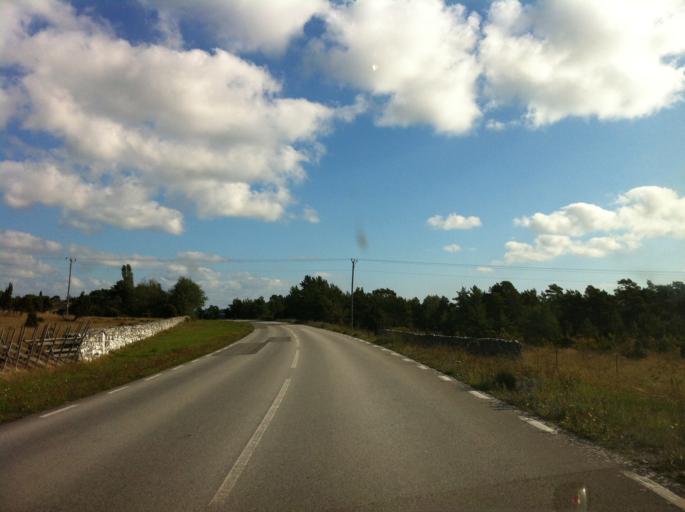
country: SE
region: Gotland
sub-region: Gotland
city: Slite
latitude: 57.9121
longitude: 19.1220
